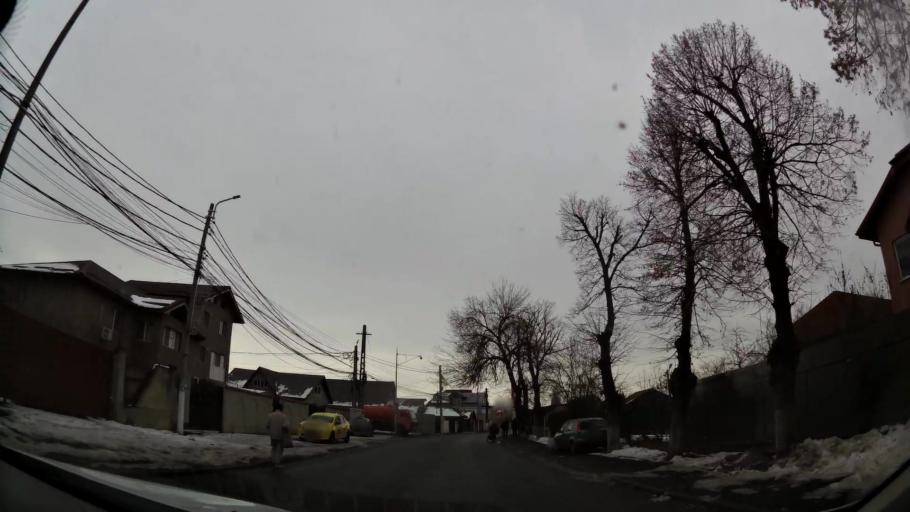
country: RO
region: Ilfov
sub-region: Comuna Pantelimon
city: Pantelimon
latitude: 44.4612
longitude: 26.2111
